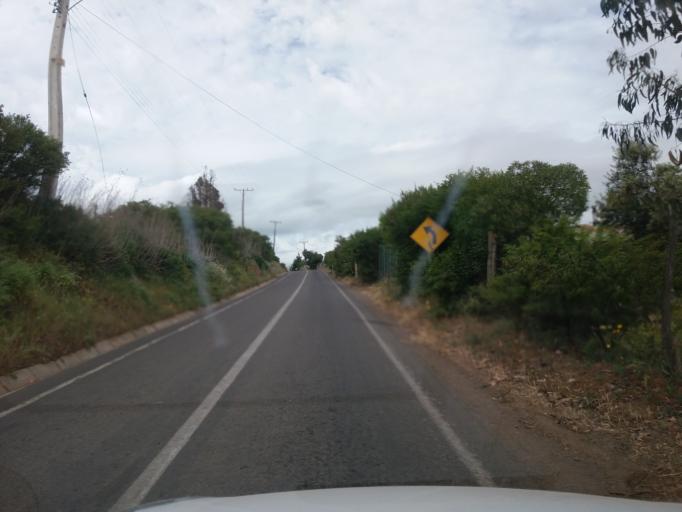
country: CL
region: Valparaiso
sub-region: Provincia de Marga Marga
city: Villa Alemana
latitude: -32.9172
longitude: -71.3858
